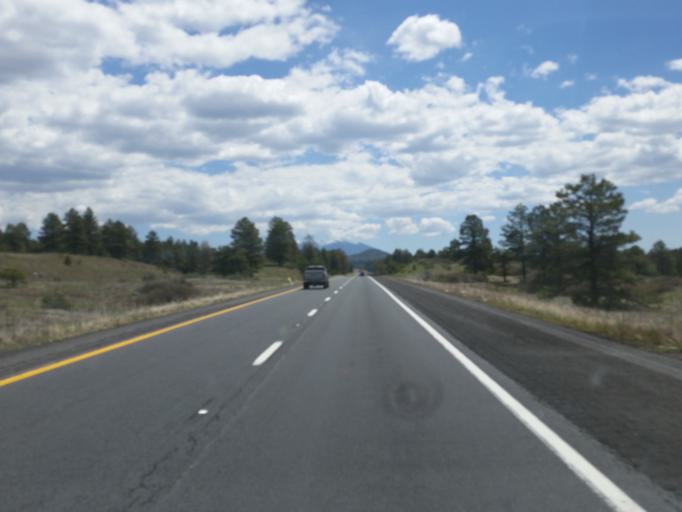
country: US
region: Arizona
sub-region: Coconino County
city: Parks
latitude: 35.2489
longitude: -111.9650
